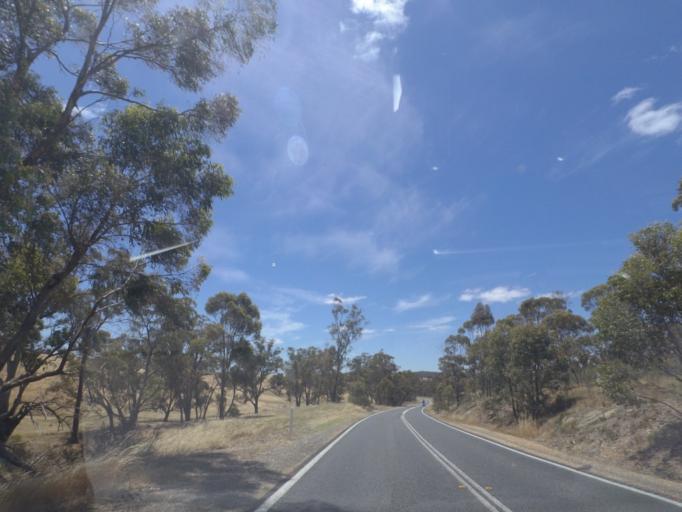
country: AU
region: Victoria
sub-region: Mount Alexander
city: Castlemaine
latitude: -37.2031
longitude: 144.1422
